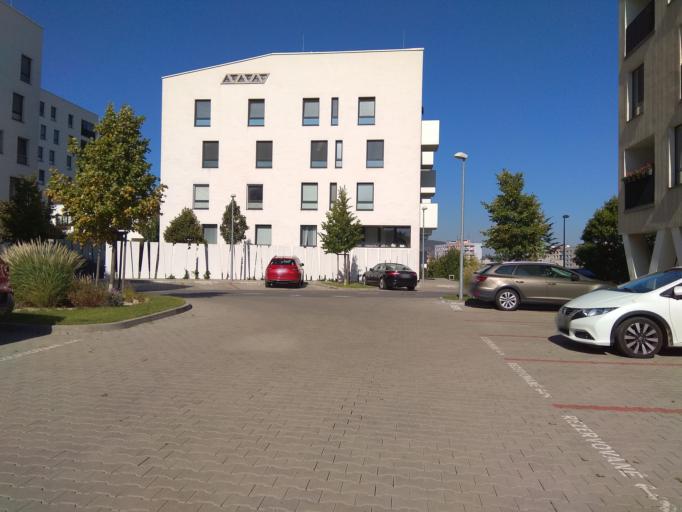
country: SK
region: Kosicky
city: Kosice
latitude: 48.7235
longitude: 21.2412
